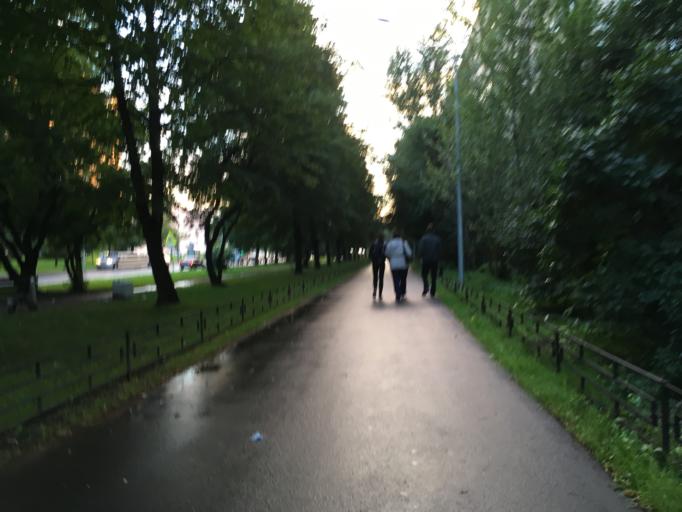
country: RU
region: Leningrad
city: Rybatskoye
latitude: 59.8929
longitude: 30.4863
